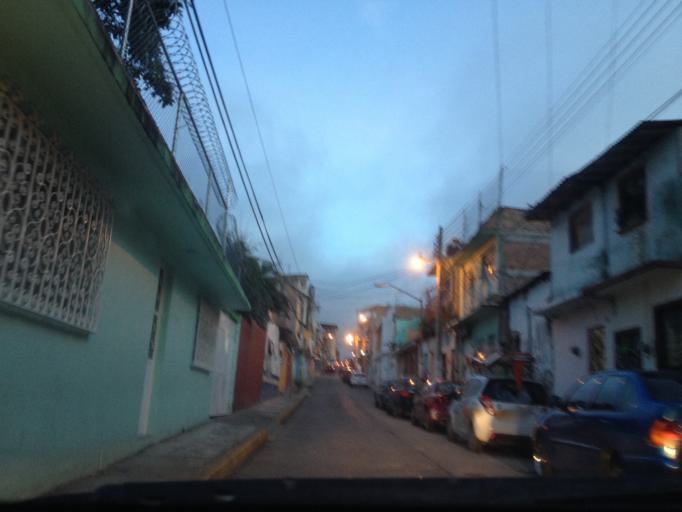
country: MX
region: Guerrero
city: Chilpancingo de los Bravos
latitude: 17.5555
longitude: -99.4986
